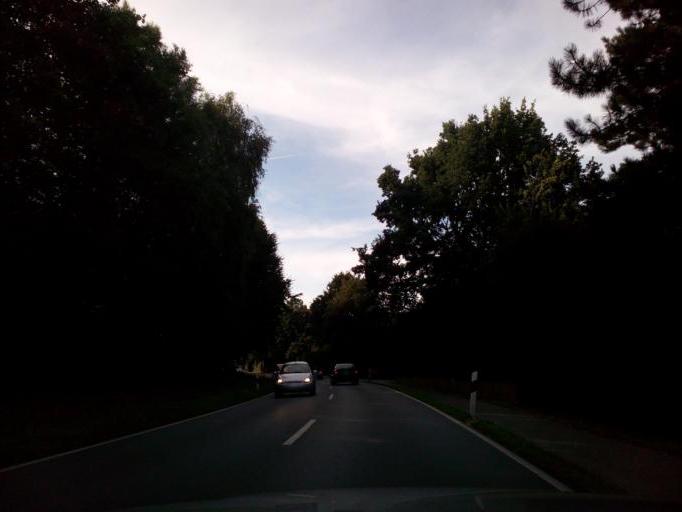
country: DE
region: North Rhine-Westphalia
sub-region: Regierungsbezirk Munster
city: Muenster
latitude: 51.9464
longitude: 7.5630
